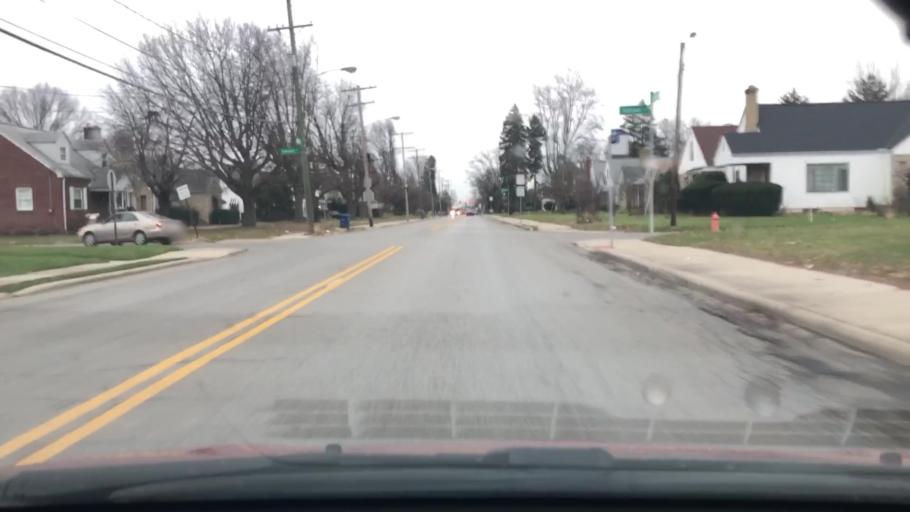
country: US
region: Ohio
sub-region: Franklin County
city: Minerva Park
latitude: 40.0315
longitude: -82.9687
